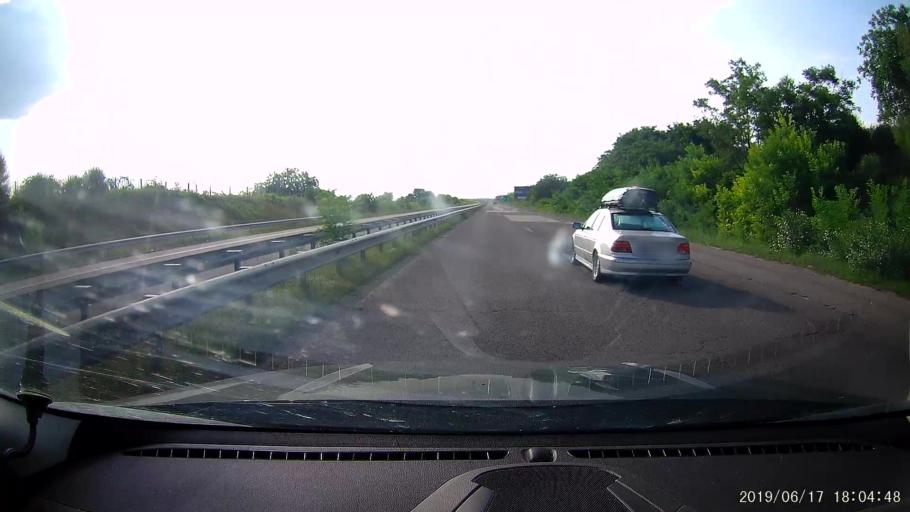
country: BG
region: Khaskovo
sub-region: Obshtina Svilengrad
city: Svilengrad
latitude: 41.7899
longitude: 26.1905
